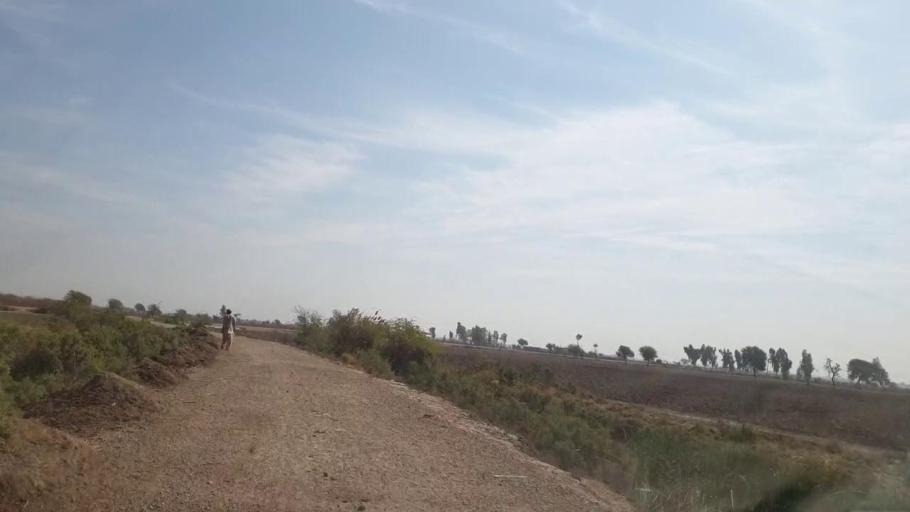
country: PK
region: Sindh
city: Mirpur Khas
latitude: 25.5760
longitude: 69.1862
